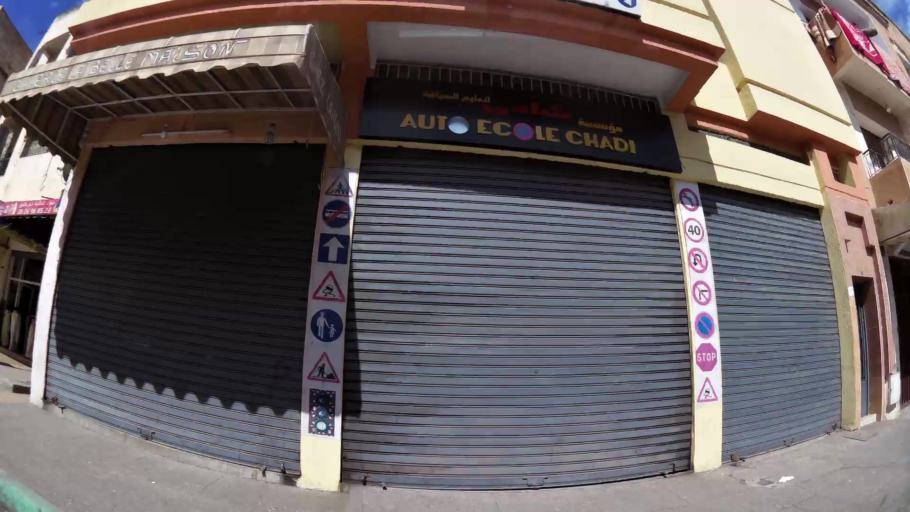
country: MA
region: Fes-Boulemane
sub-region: Fes
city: Fes
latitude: 34.0321
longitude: -5.0242
